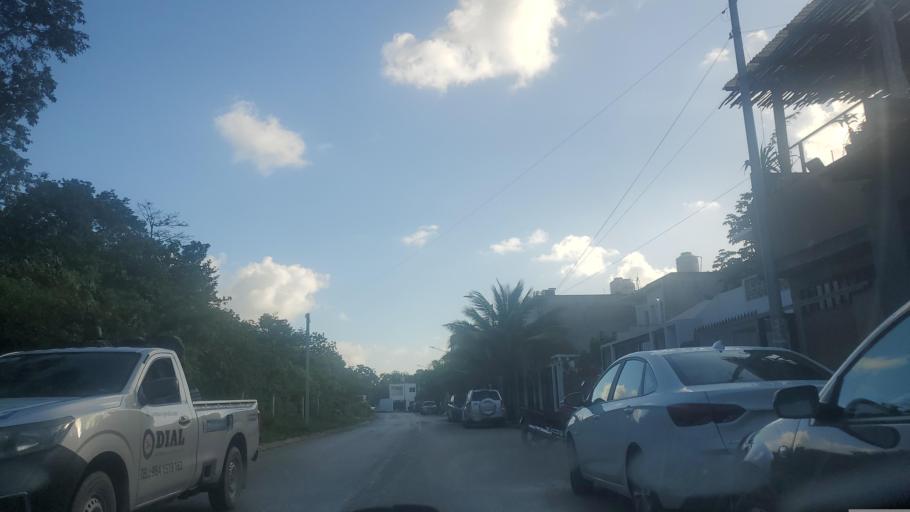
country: MX
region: Quintana Roo
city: Tulum
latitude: 20.2162
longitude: -87.4576
